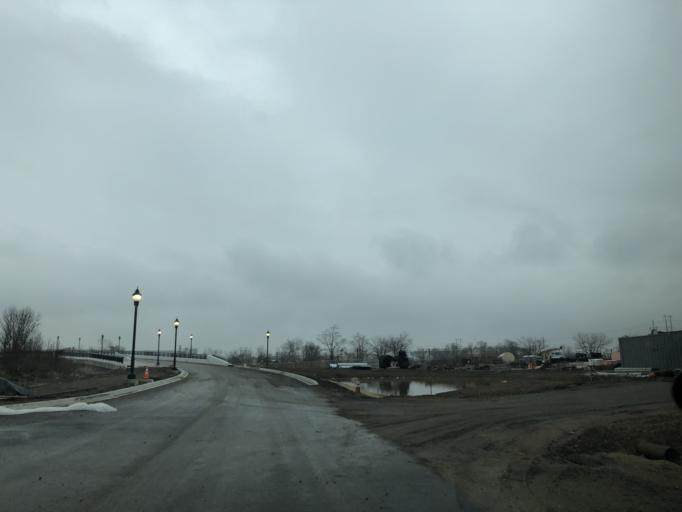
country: US
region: Delaware
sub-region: New Castle County
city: Wilmington
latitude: 39.7277
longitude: -75.5633
